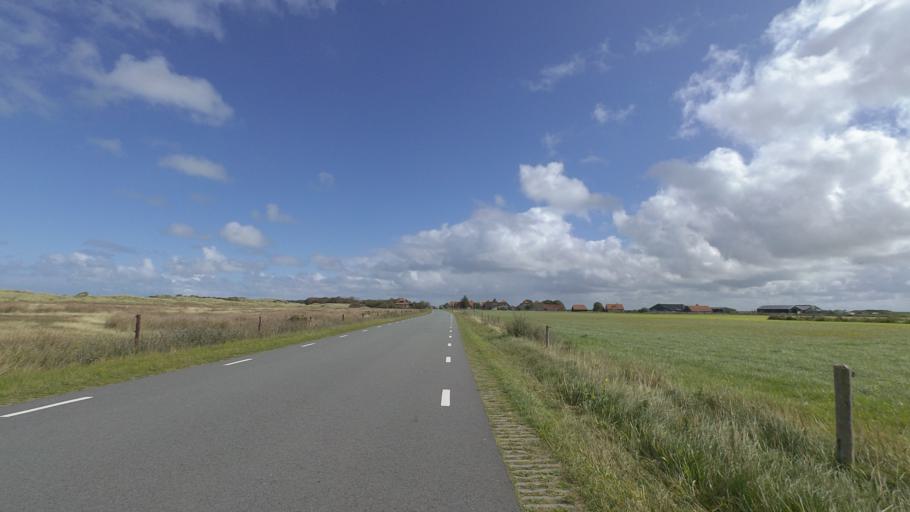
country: NL
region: Friesland
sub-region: Gemeente Ameland
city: Nes
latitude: 53.4500
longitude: 5.8325
